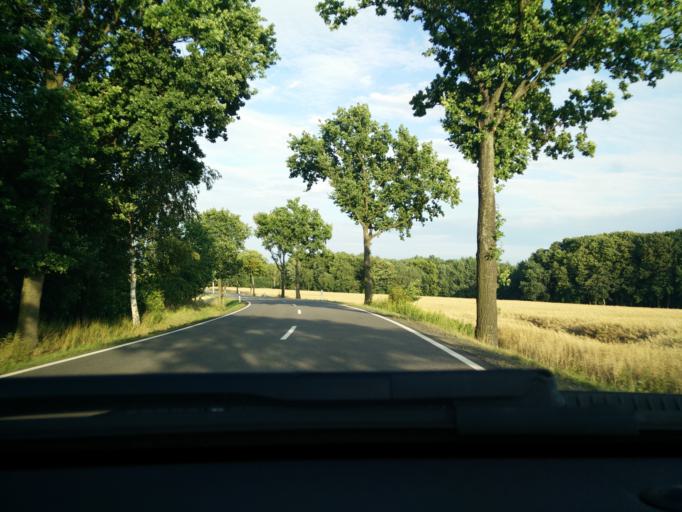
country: DE
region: Saxony
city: Konigsfeld
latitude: 51.0697
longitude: 12.7363
